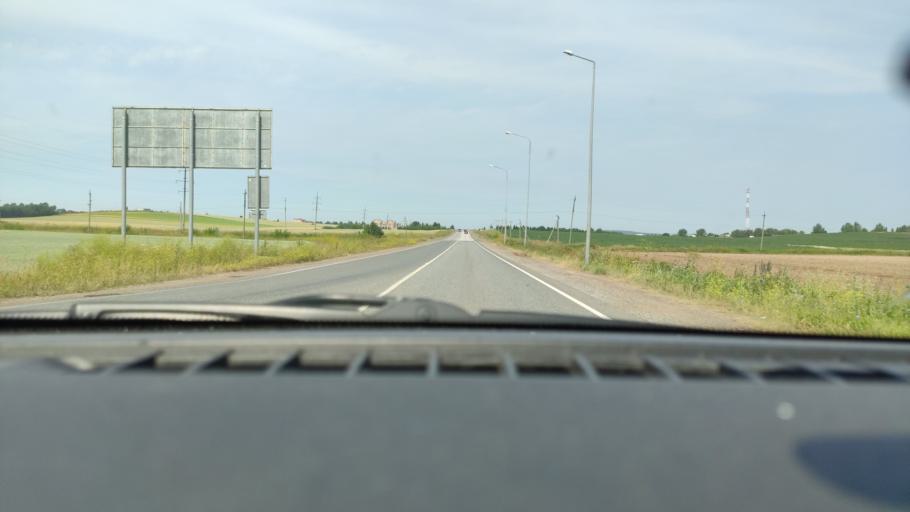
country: RU
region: Perm
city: Lobanovo
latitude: 57.8514
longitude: 56.2963
